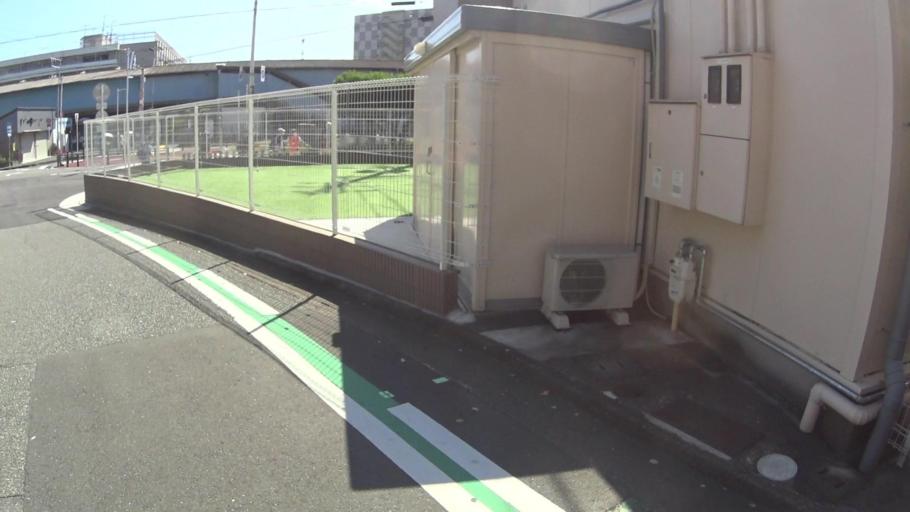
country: JP
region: Osaka
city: Sakai
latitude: 34.5429
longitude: 135.4676
